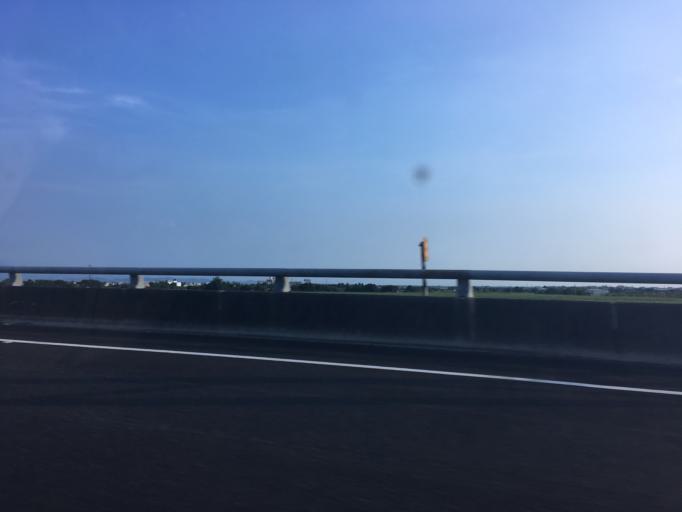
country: TW
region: Taiwan
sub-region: Chiayi
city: Taibao
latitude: 23.4255
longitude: 120.3518
